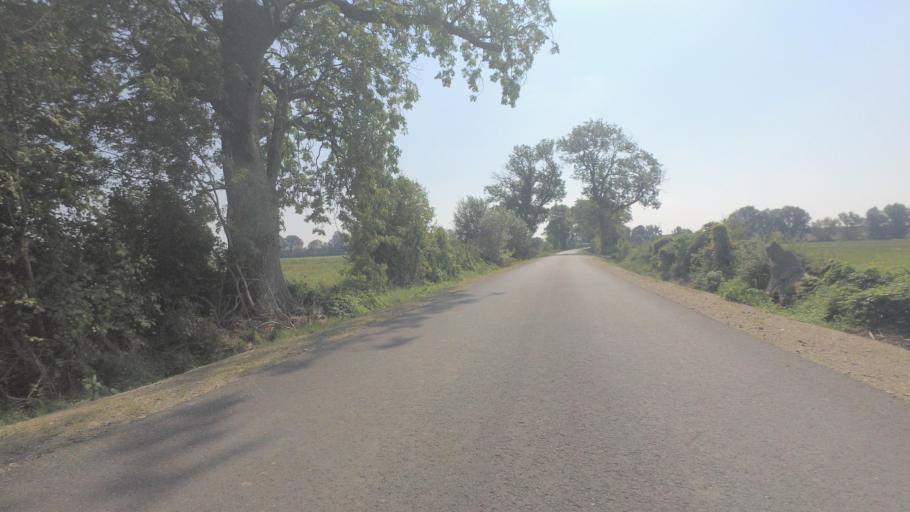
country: DE
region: Mecklenburg-Vorpommern
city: Gielow
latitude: 53.7231
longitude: 12.6812
